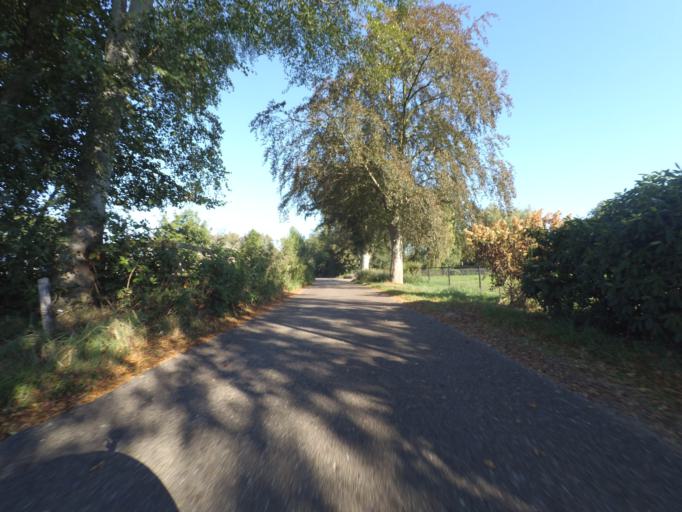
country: NL
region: Gelderland
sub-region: Gemeente Barneveld
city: Barneveld
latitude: 52.1783
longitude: 5.5614
